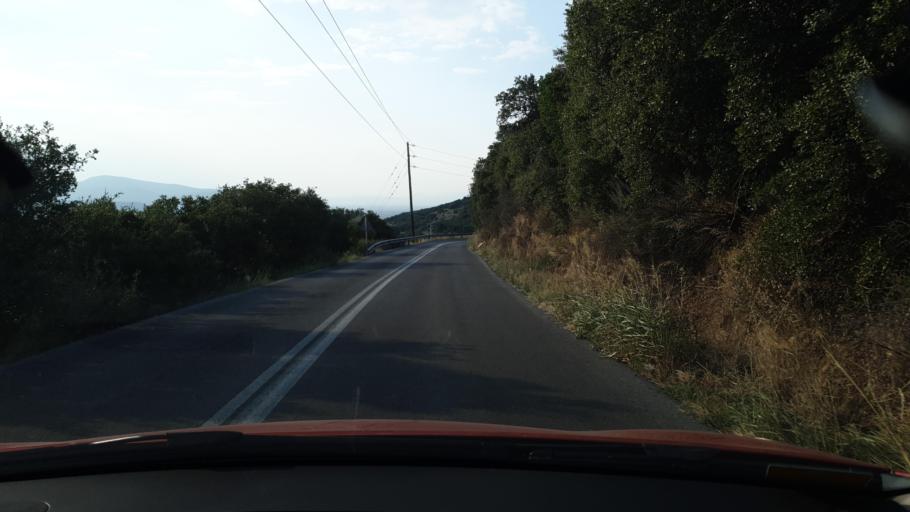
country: GR
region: Thessaly
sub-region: Nomos Magnisias
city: Pteleos
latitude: 39.0621
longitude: 22.9290
